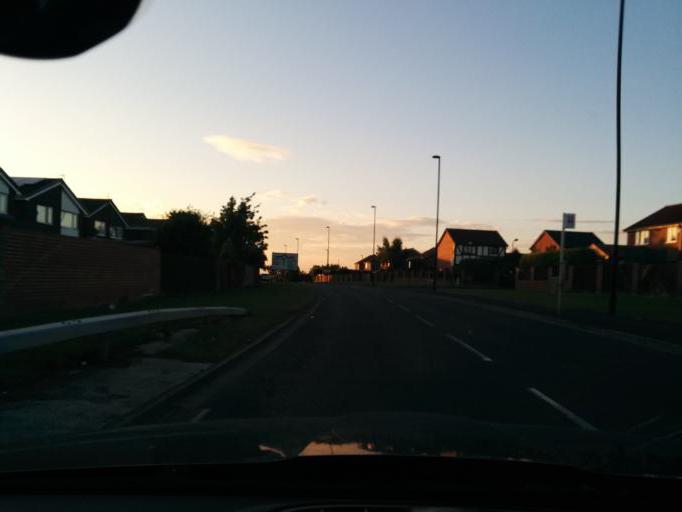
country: GB
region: England
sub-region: Northumberland
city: Seghill
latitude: 55.0403
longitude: -1.5641
